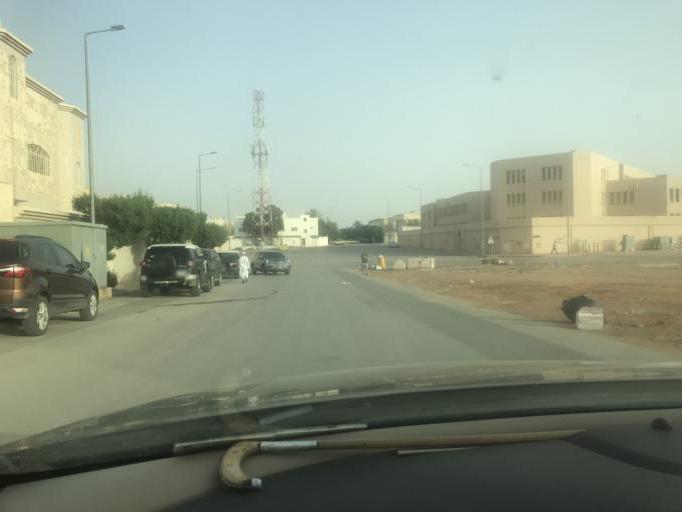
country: SA
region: Ar Riyad
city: Riyadh
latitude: 24.7424
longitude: 46.7742
